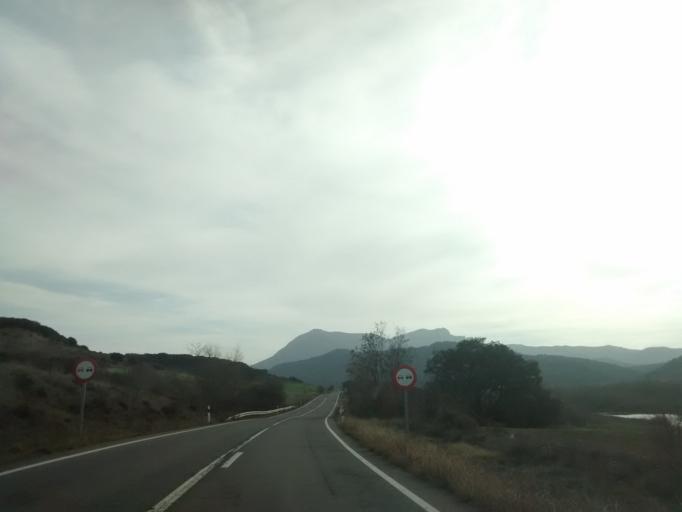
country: ES
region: Aragon
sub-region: Provincia de Huesca
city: Bailo
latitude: 42.5686
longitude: -0.8087
